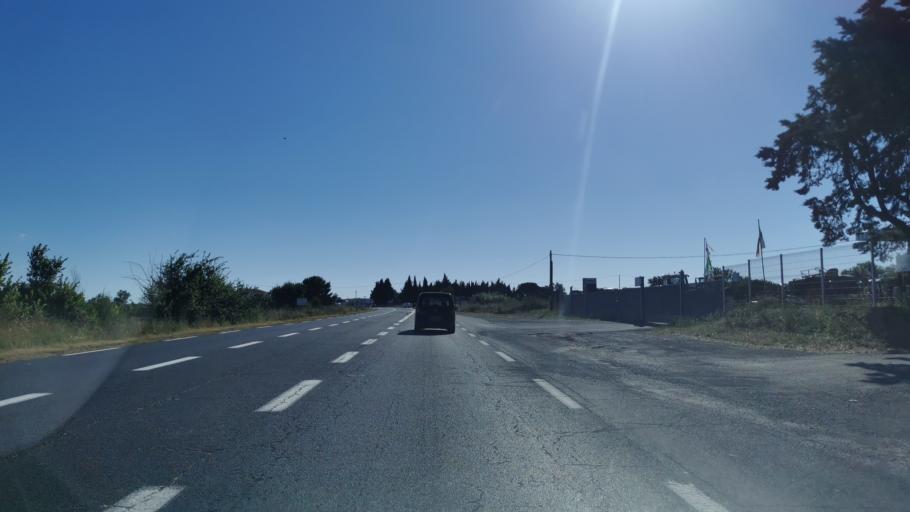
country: FR
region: Languedoc-Roussillon
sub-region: Departement de l'Herault
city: Colombiers
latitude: 43.2967
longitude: 3.1464
